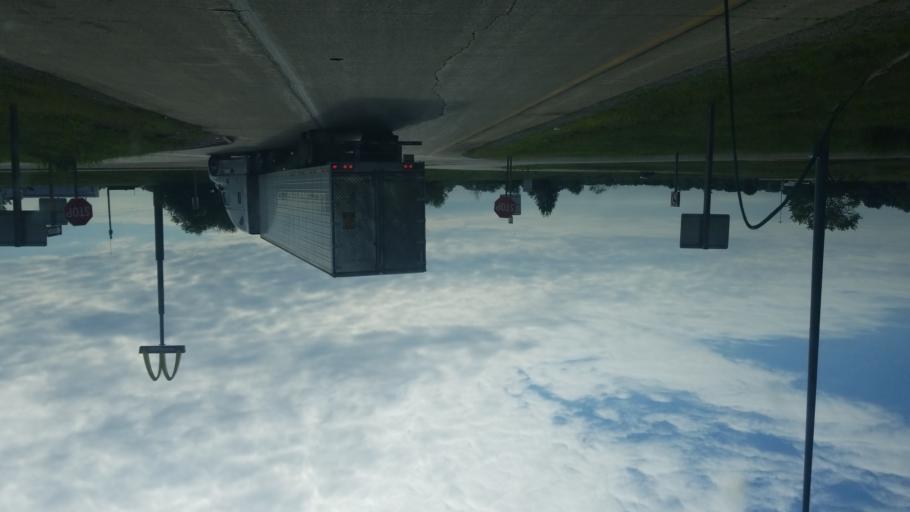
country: US
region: Illinois
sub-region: Clark County
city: Marshall
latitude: 39.4197
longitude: -87.6941
